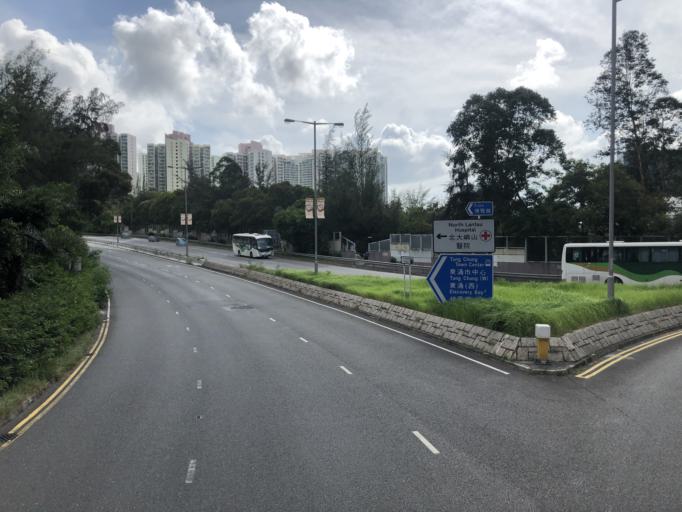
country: HK
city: Tai O
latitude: 22.2889
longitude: 113.9475
